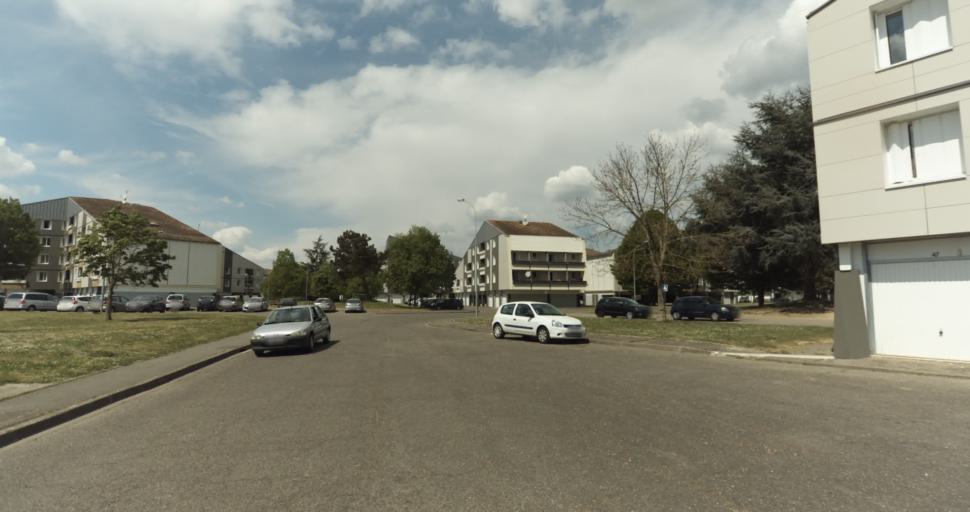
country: FR
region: Aquitaine
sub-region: Departement du Lot-et-Garonne
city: Agen
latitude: 44.1895
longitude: 0.6346
